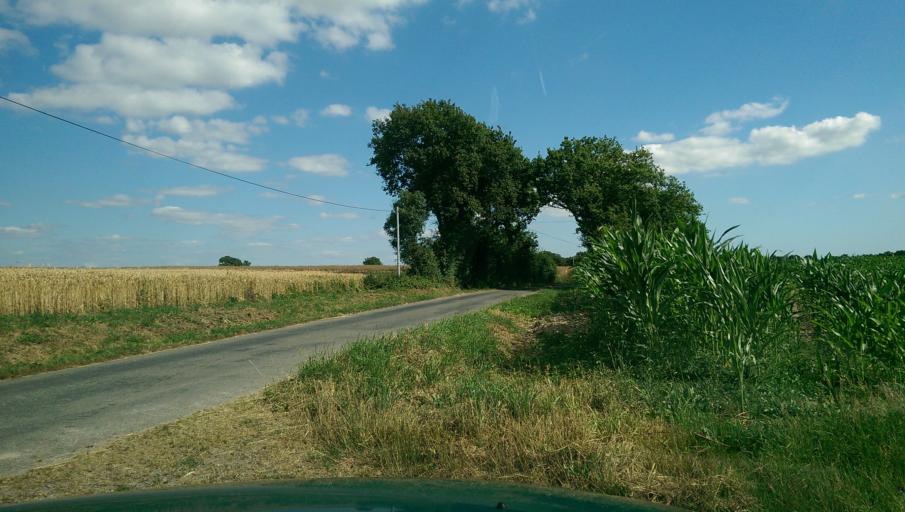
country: FR
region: Pays de la Loire
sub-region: Departement de la Loire-Atlantique
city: Lege
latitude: 46.8982
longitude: -1.5672
